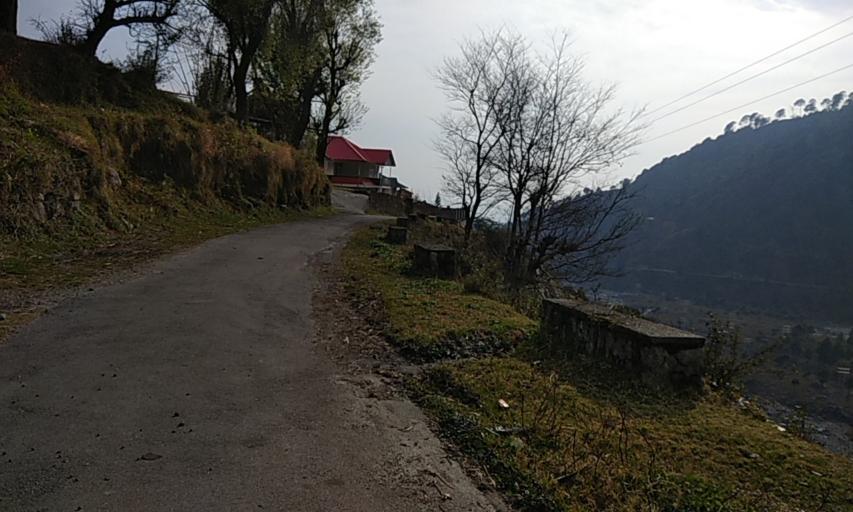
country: IN
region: Himachal Pradesh
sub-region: Kangra
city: Palampur
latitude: 32.1399
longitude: 76.5377
